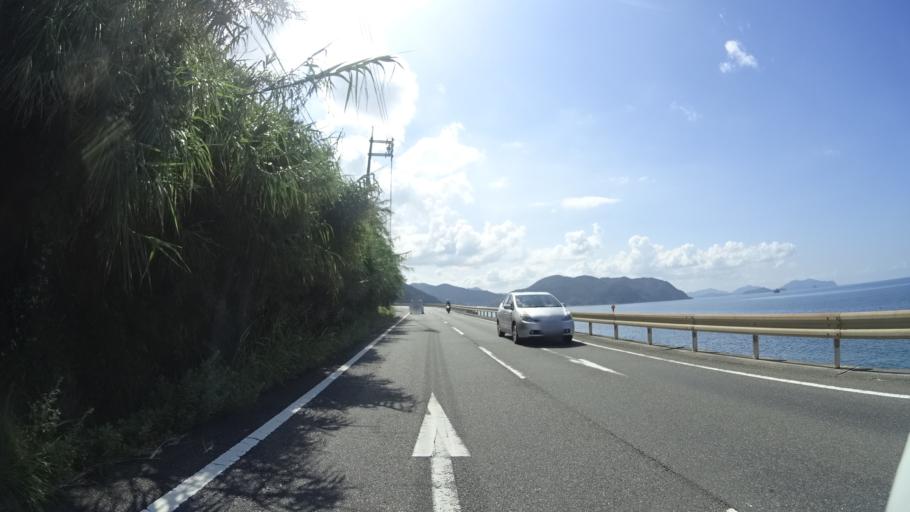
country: JP
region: Yamaguchi
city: Shimonoseki
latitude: 34.2437
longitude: 130.9164
